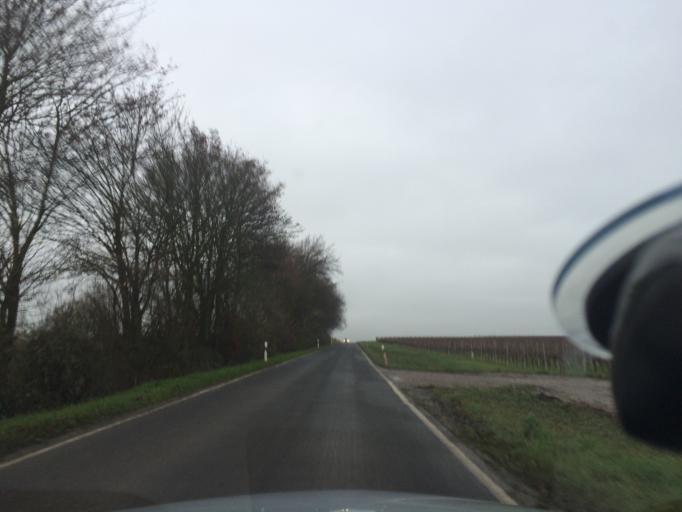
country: DE
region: Rheinland-Pfalz
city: Gabsheim
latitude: 49.8135
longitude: 8.1759
